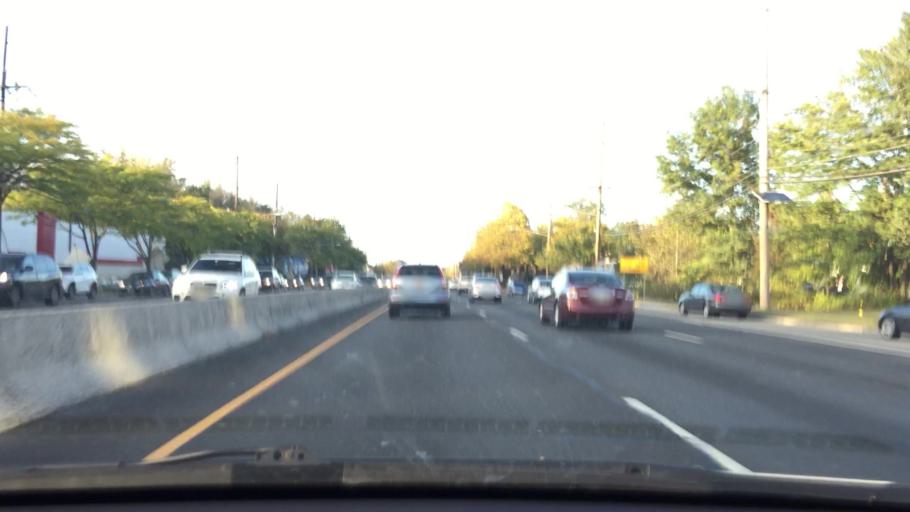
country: US
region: New Jersey
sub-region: Bergen County
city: Paramus
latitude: 40.9420
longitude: -74.0715
